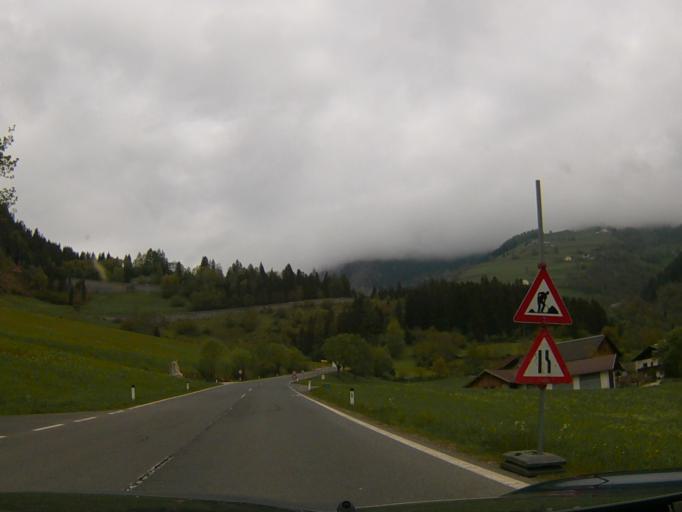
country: AT
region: Carinthia
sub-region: Politischer Bezirk Spittal an der Drau
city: Obervellach
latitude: 46.9627
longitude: 13.1851
